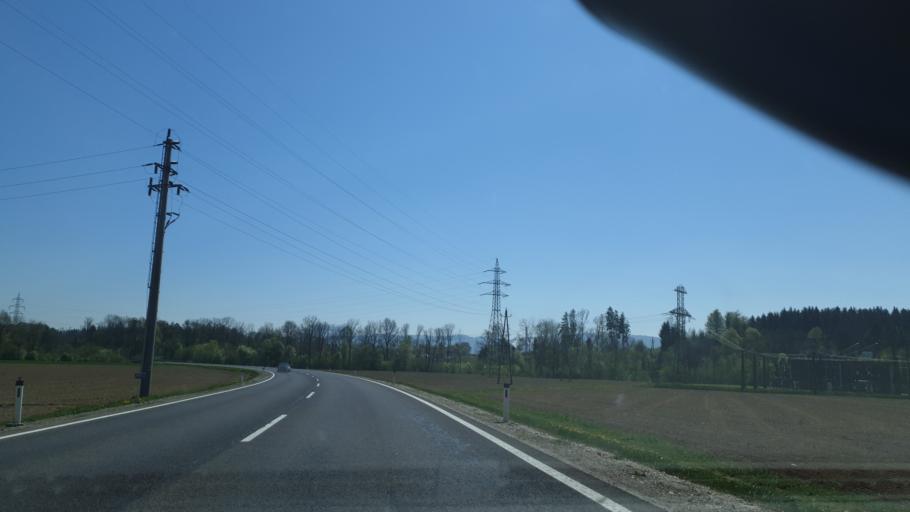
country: AT
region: Upper Austria
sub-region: Politischer Bezirk Vocklabruck
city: Timelkam
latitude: 47.9955
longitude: 13.5992
